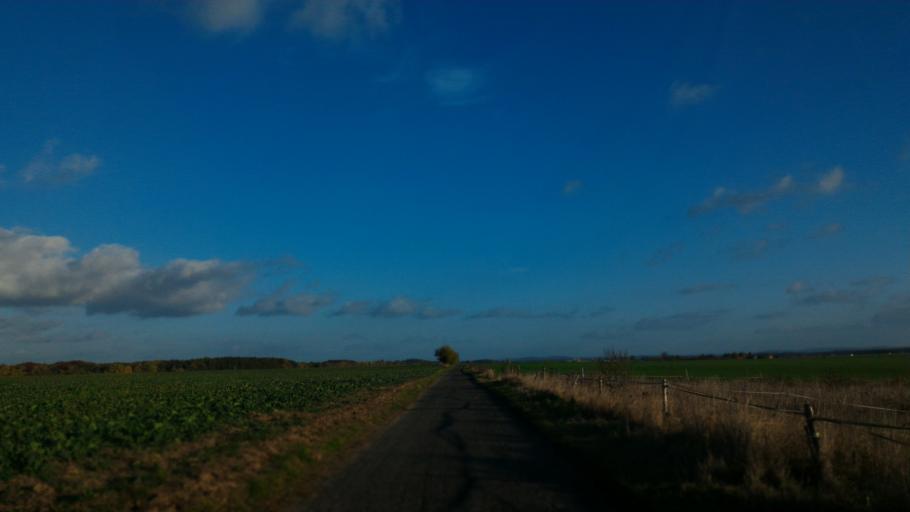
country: CZ
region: Central Bohemia
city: Bela pod Bezdezem
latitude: 50.5245
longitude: 14.7443
